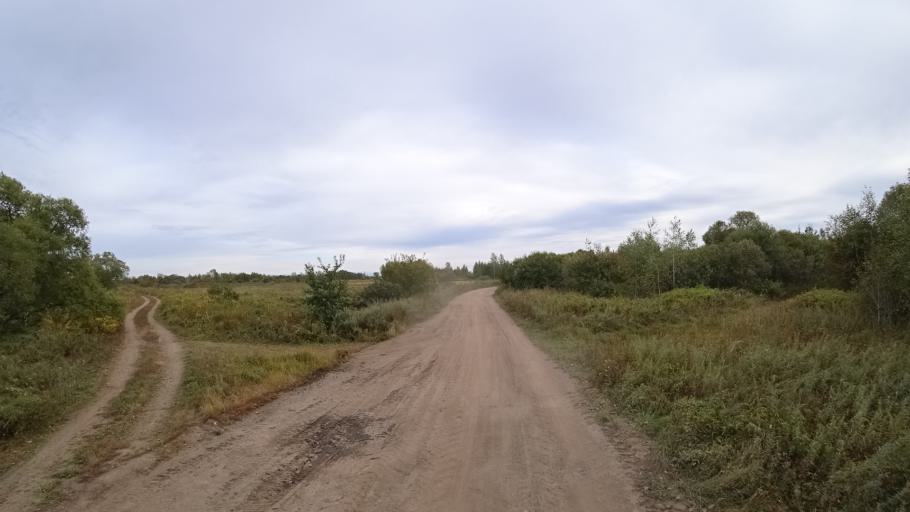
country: RU
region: Amur
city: Arkhara
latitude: 49.3431
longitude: 130.1031
